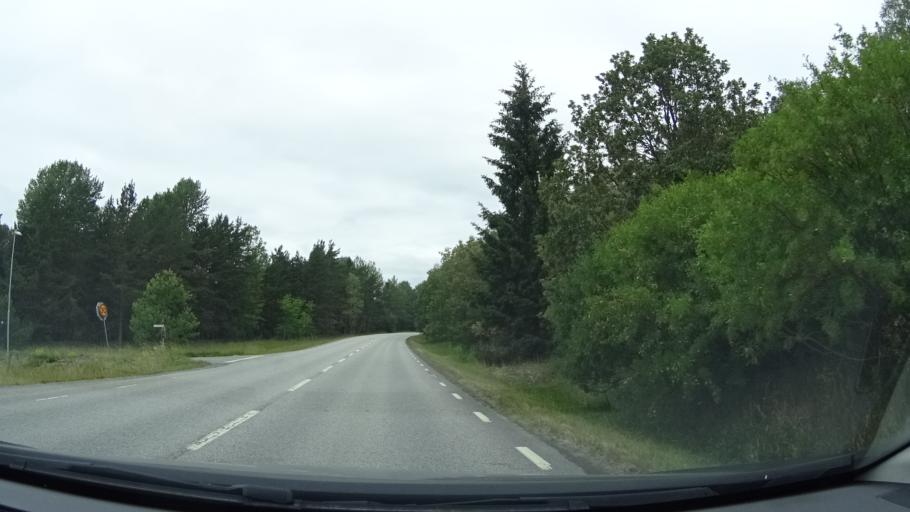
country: SE
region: Stockholm
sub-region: Varmdo Kommun
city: Hemmesta
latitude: 59.3405
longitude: 18.4842
